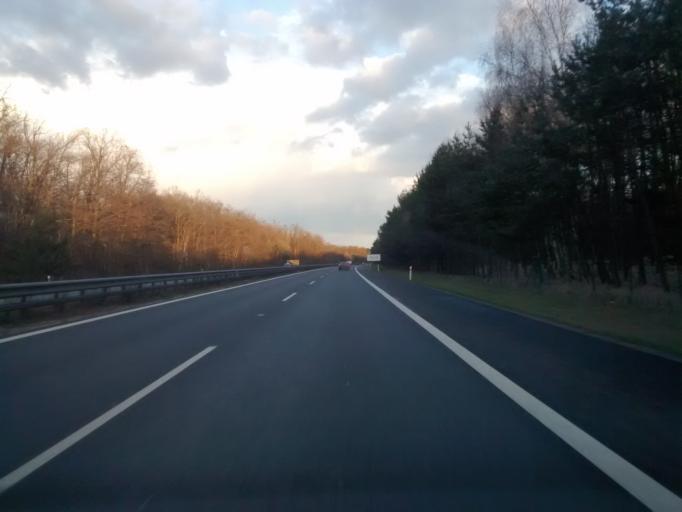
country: CZ
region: Central Bohemia
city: Poricany
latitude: 50.1261
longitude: 14.9161
